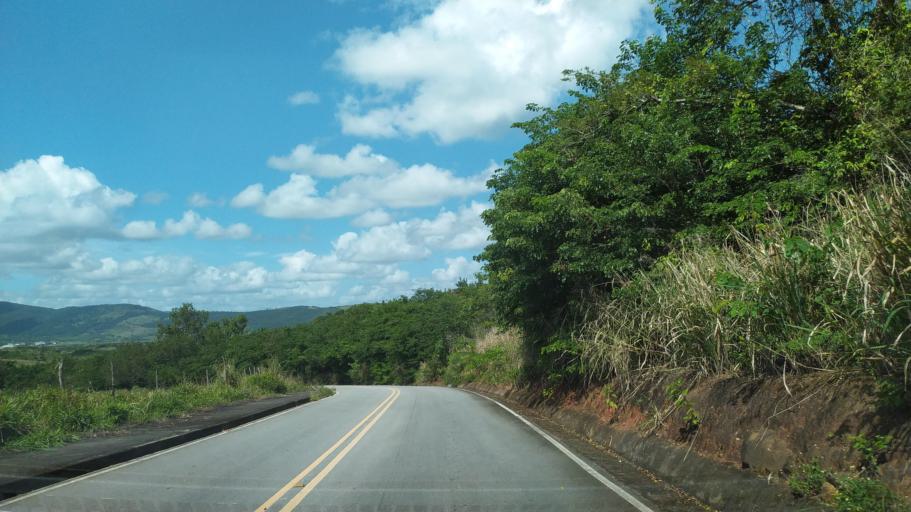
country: BR
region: Alagoas
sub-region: Uniao Dos Palmares
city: Uniao dos Palmares
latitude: -9.1684
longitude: -36.0630
